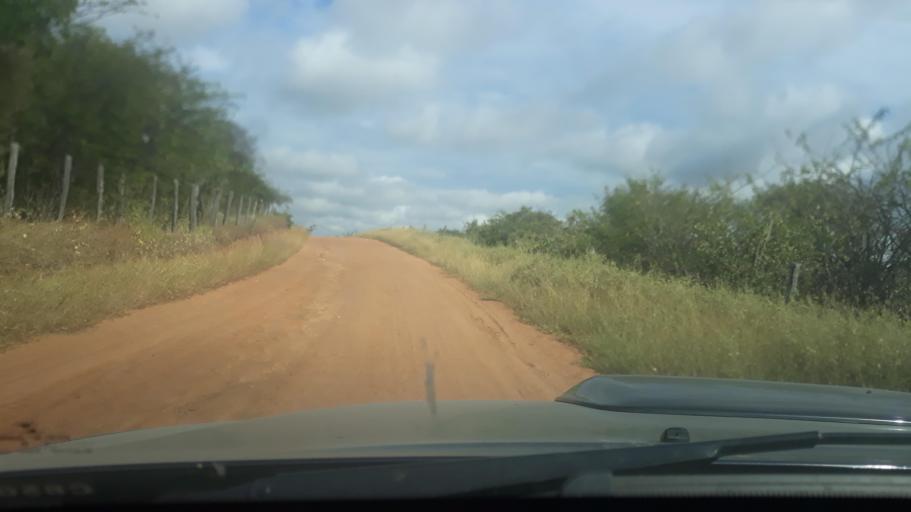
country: BR
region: Bahia
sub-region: Riacho De Santana
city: Riacho de Santana
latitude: -13.8995
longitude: -42.8738
